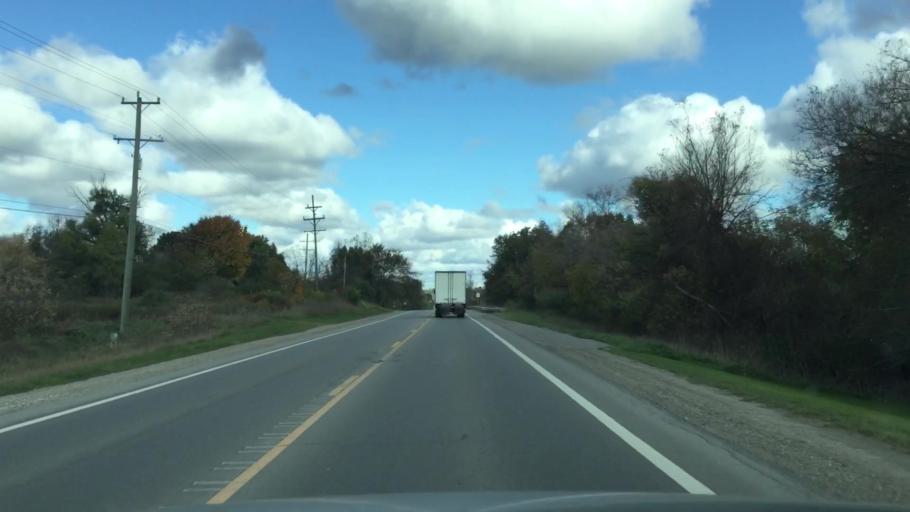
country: US
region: Michigan
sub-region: Oakland County
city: Oxford
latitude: 42.9074
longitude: -83.3122
